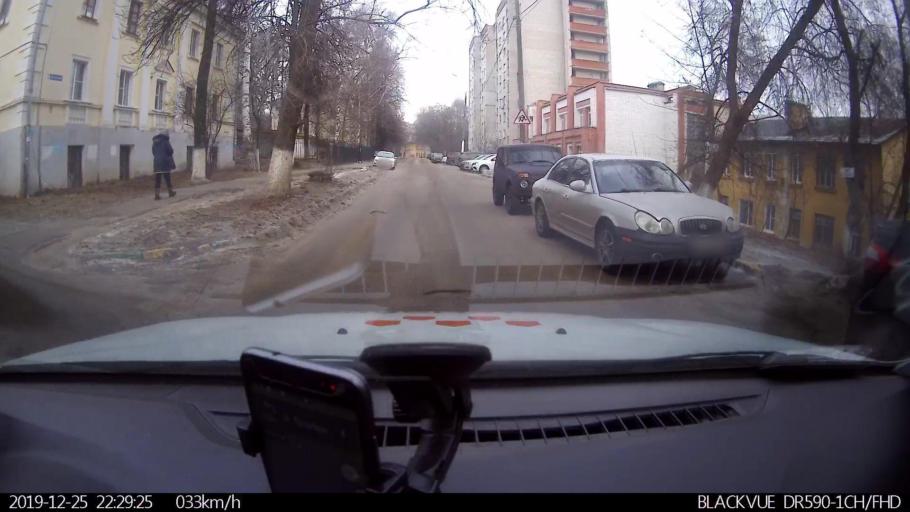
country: RU
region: Nizjnij Novgorod
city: Nizhniy Novgorod
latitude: 56.2672
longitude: 43.9844
